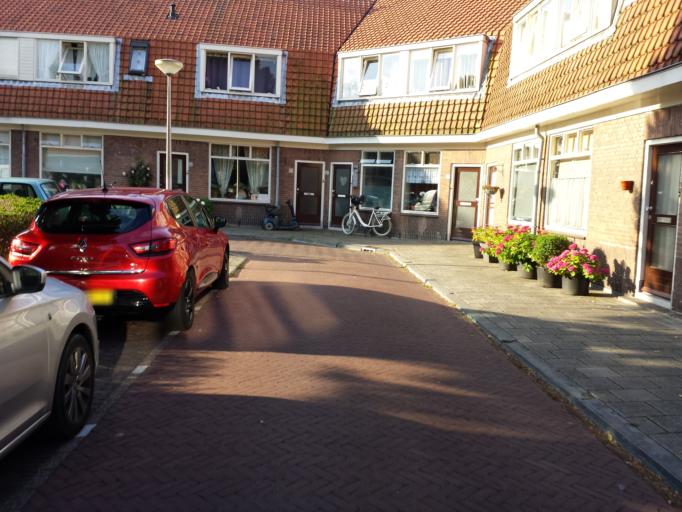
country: NL
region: South Holland
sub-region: Gemeente Delft
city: Delft
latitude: 52.0080
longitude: 4.3757
